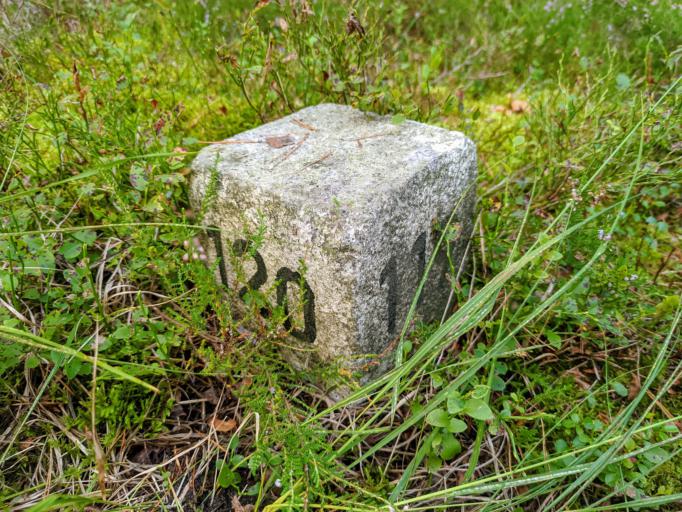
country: PL
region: Lubusz
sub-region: Powiat nowosolski
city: Siedlisko
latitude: 51.8284
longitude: 15.8775
